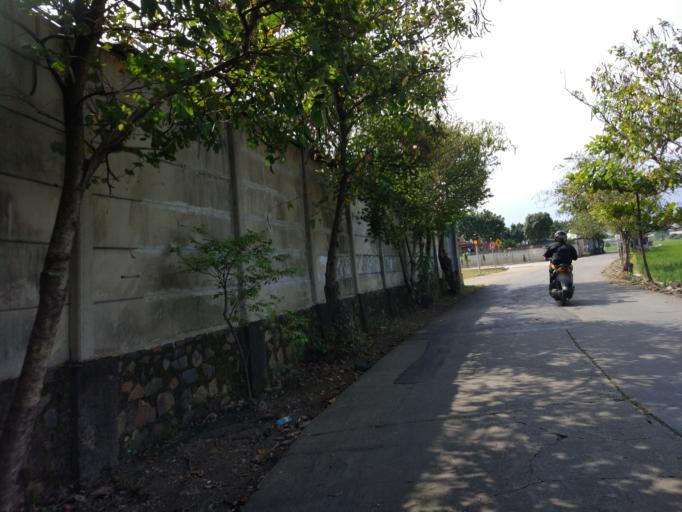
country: ID
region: West Java
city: Cileunyi
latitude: -6.9345
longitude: 107.7061
